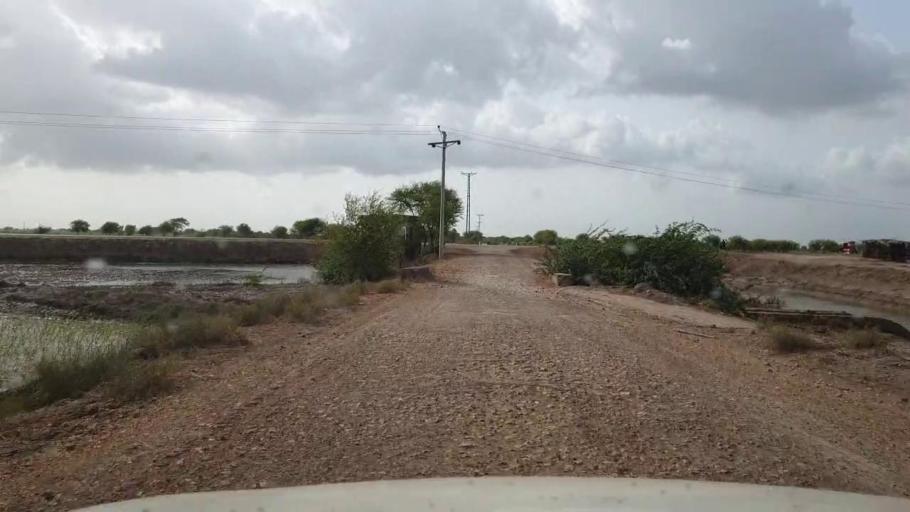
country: PK
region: Sindh
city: Kario
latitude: 24.7810
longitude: 68.5882
